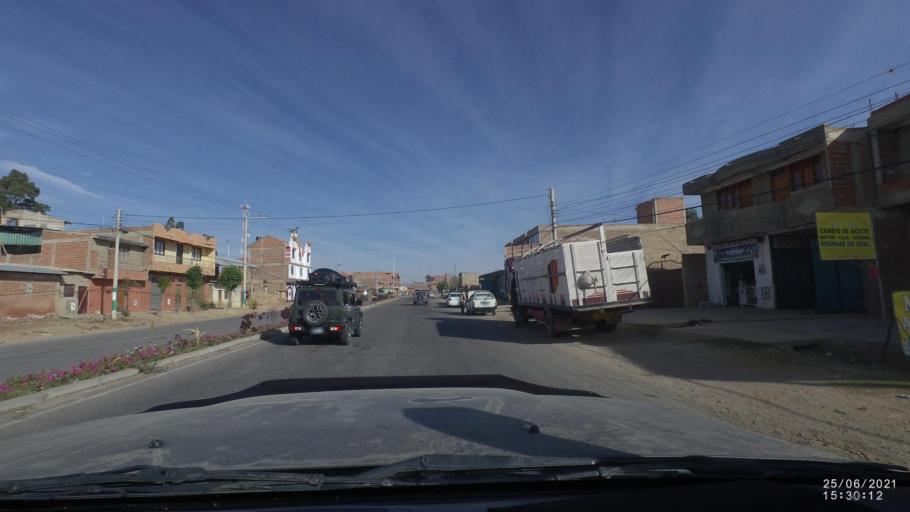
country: BO
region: Cochabamba
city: Cliza
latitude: -17.5816
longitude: -65.9337
